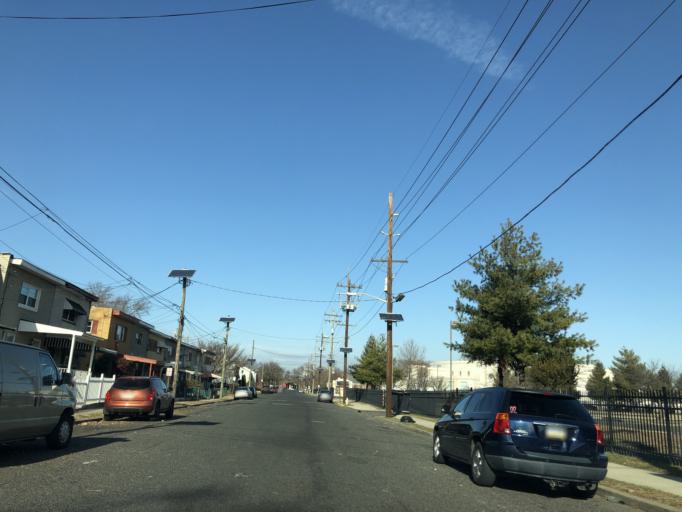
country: US
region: New Jersey
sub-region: Camden County
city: Camden
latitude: 39.9251
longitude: -75.1124
